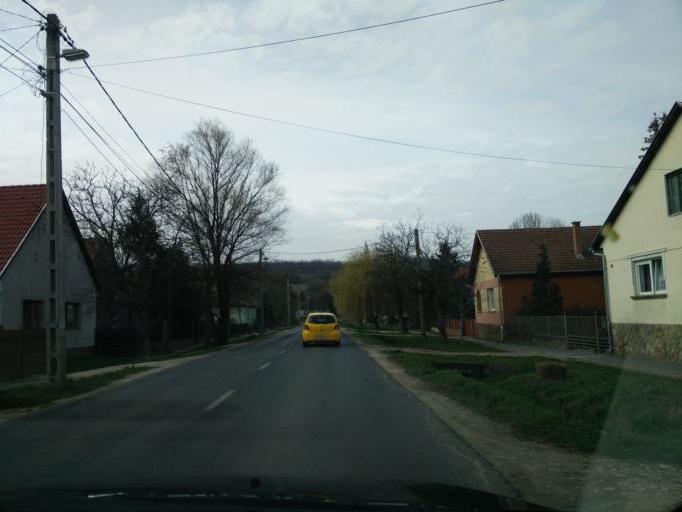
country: HU
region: Pest
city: Piliscsaba
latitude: 47.6310
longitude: 18.8245
